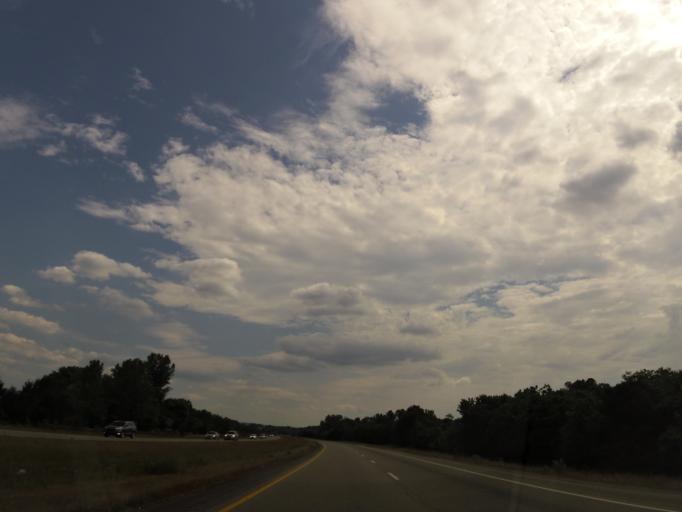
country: US
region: Tennessee
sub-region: Marion County
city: South Pittsburg
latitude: 35.0094
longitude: -85.7013
